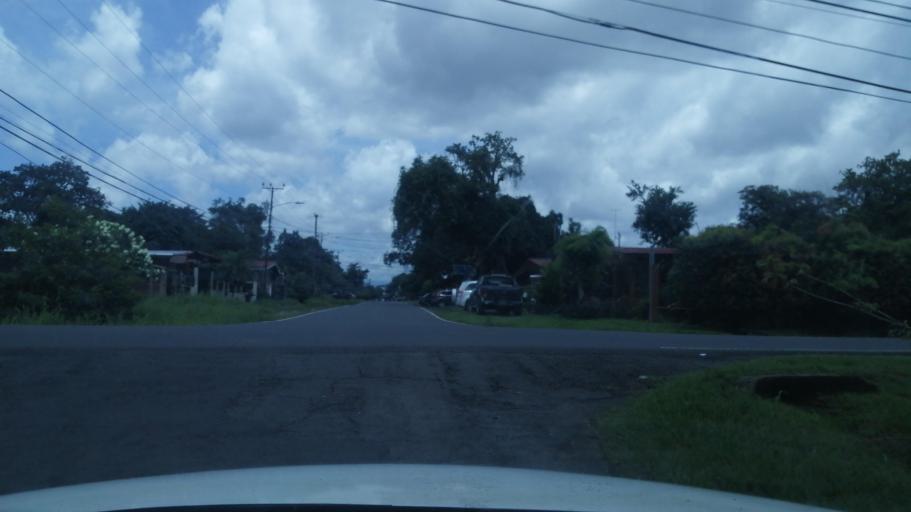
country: PA
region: Chiriqui
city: David
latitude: 8.4242
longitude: -82.4394
